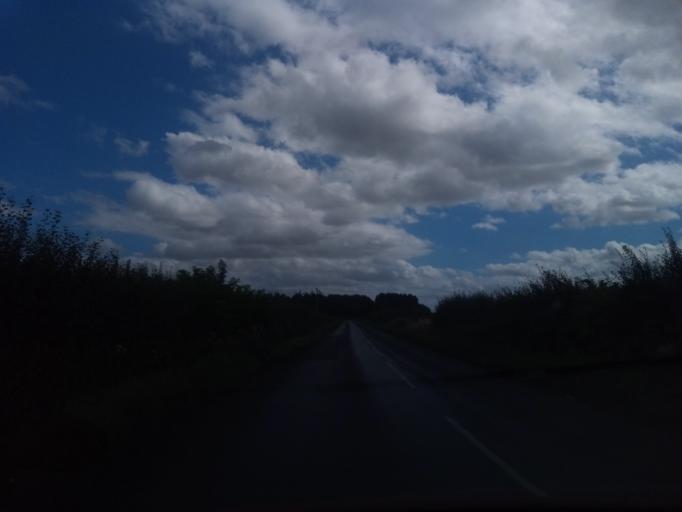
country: GB
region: Scotland
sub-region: The Scottish Borders
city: Coldstream
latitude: 55.6423
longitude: -2.3034
